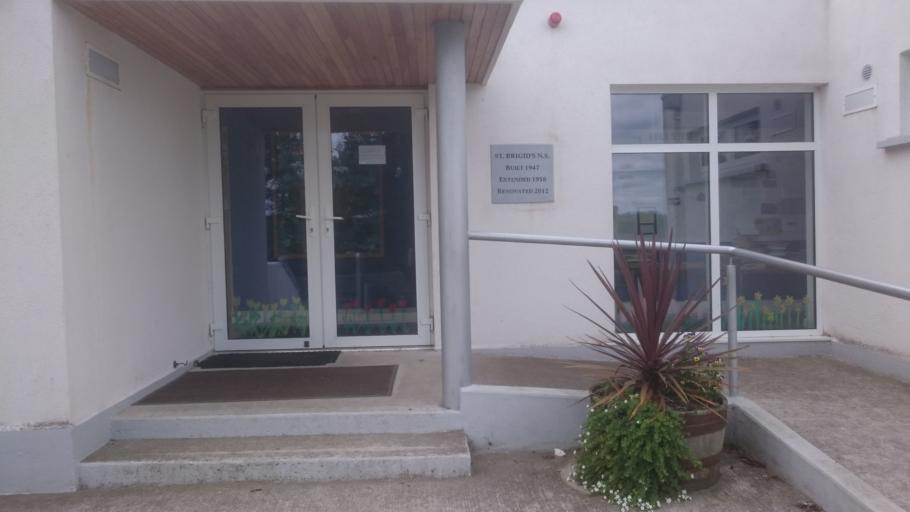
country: IE
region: Leinster
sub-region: Kilkenny
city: Kilkenny
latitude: 52.5388
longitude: -7.2716
